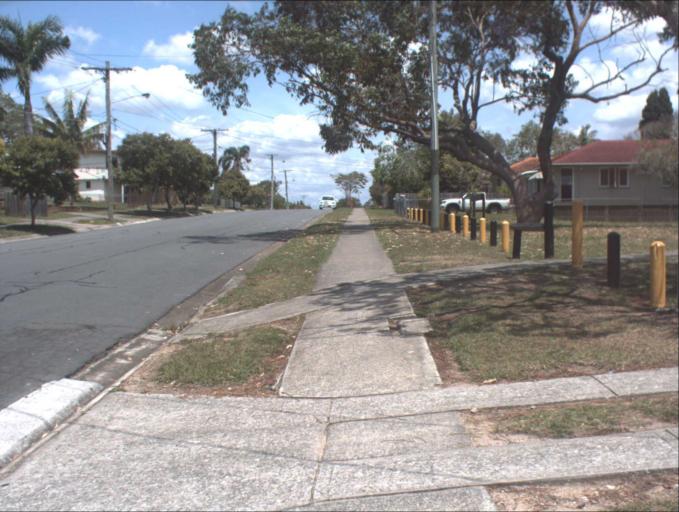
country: AU
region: Queensland
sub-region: Logan
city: Woodridge
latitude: -27.6268
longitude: 153.1026
